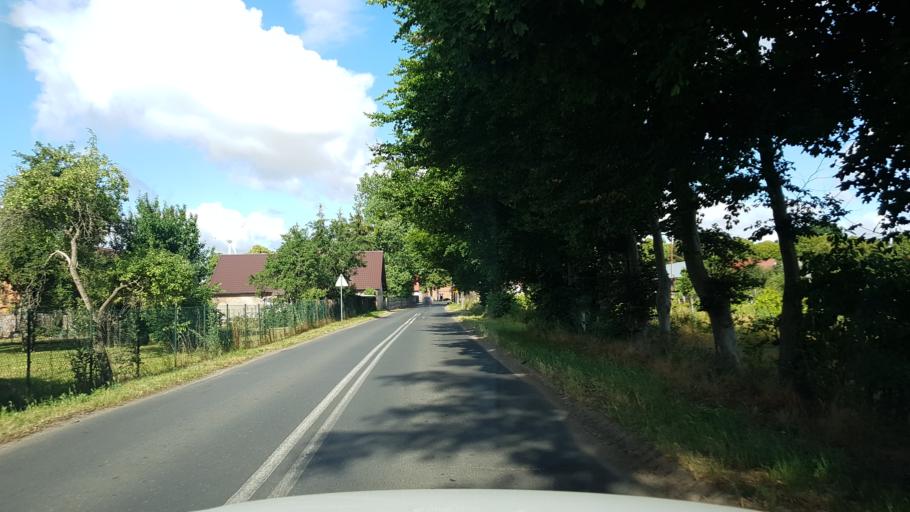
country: PL
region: West Pomeranian Voivodeship
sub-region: Powiat mysliborski
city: Debno
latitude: 52.7369
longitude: 14.6693
